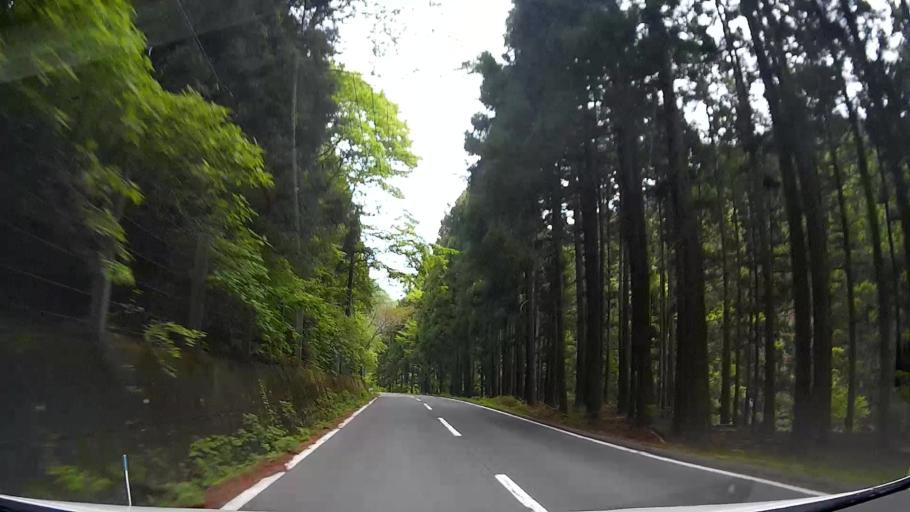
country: JP
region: Shizuoka
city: Ito
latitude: 34.9188
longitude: 139.0442
